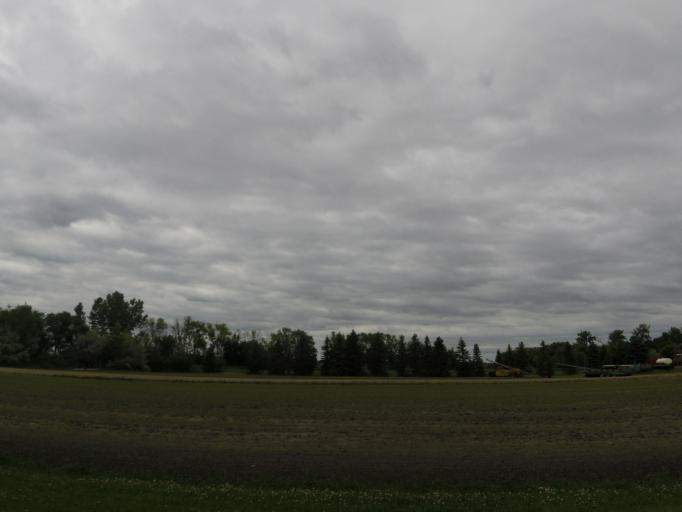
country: US
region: North Dakota
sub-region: Walsh County
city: Grafton
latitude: 48.6210
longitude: -97.4548
